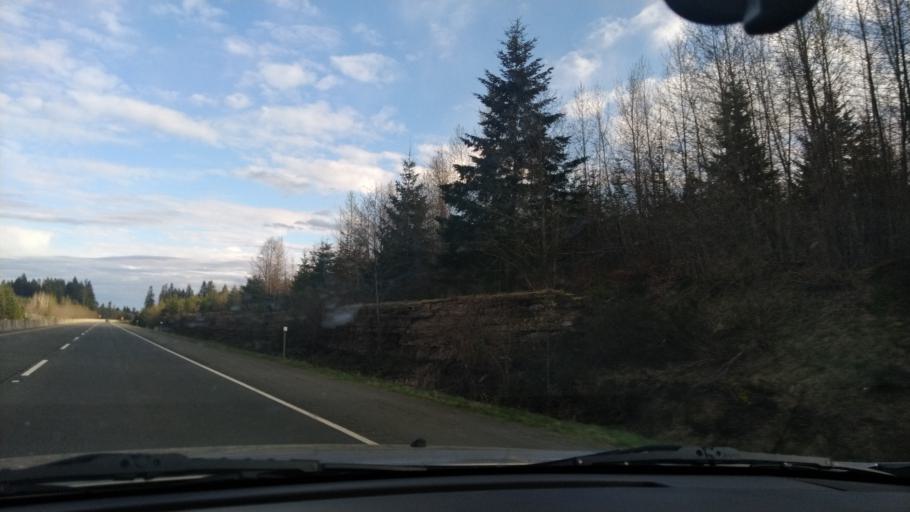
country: CA
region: British Columbia
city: Courtenay
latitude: 49.7683
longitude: -125.1373
